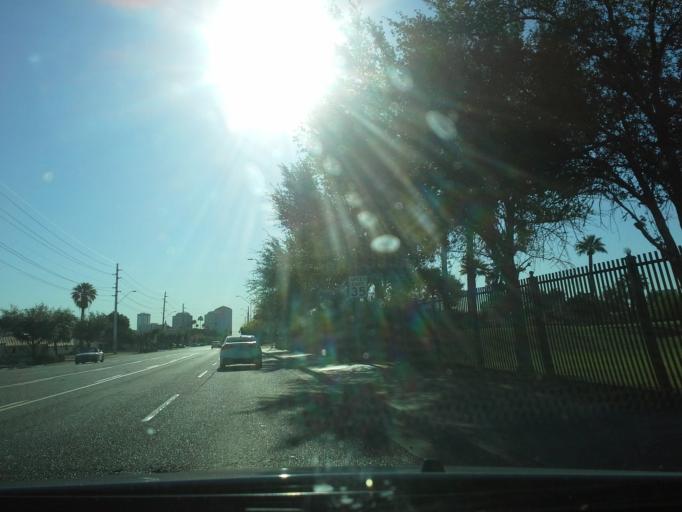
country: US
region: Arizona
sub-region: Maricopa County
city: Phoenix
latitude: 33.4804
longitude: -112.0948
